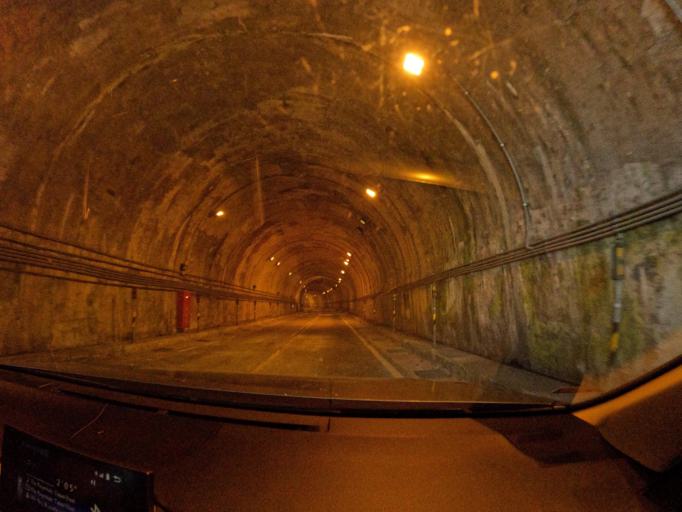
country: TW
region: Taiwan
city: Yujing
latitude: 23.2828
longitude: 120.8872
